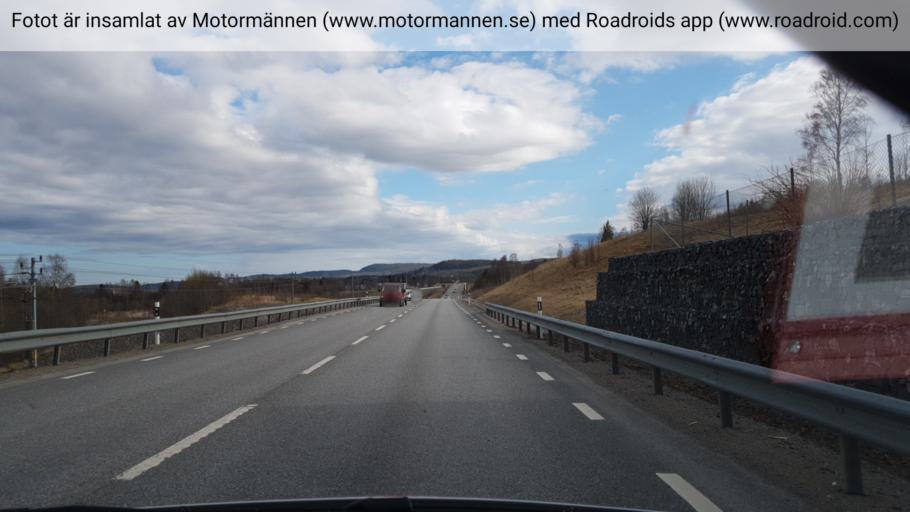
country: SE
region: Vaesternorrland
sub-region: Kramfors Kommun
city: Bollstabruk
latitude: 63.0094
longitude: 17.6733
